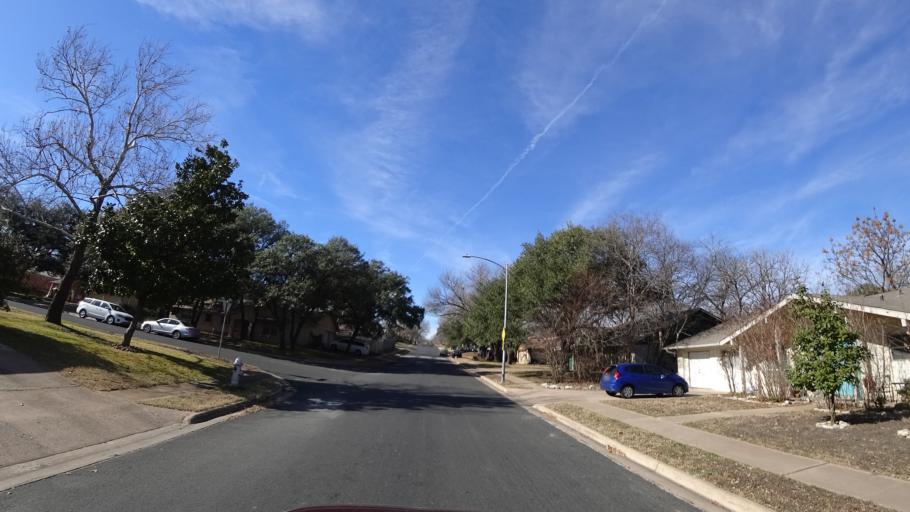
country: US
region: Texas
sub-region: Travis County
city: Wells Branch
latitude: 30.3716
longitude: -97.7057
